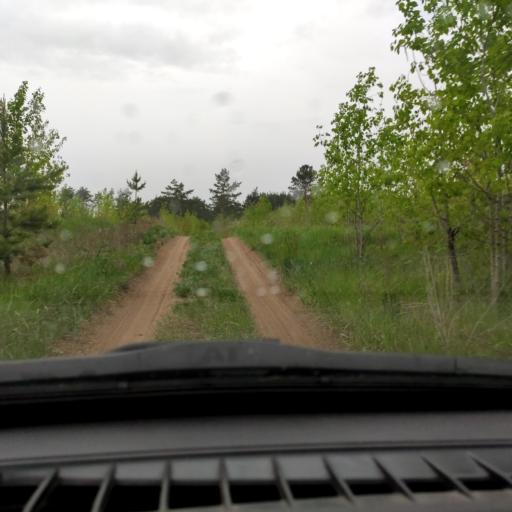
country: RU
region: Samara
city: Zhigulevsk
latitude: 53.5211
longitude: 49.5458
